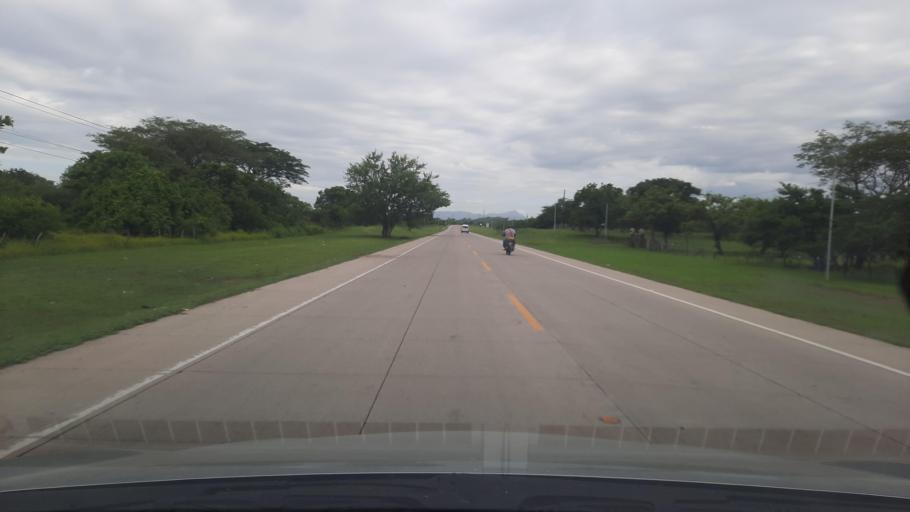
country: NI
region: Chinandega
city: Somotillo
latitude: 12.8936
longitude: -86.8506
